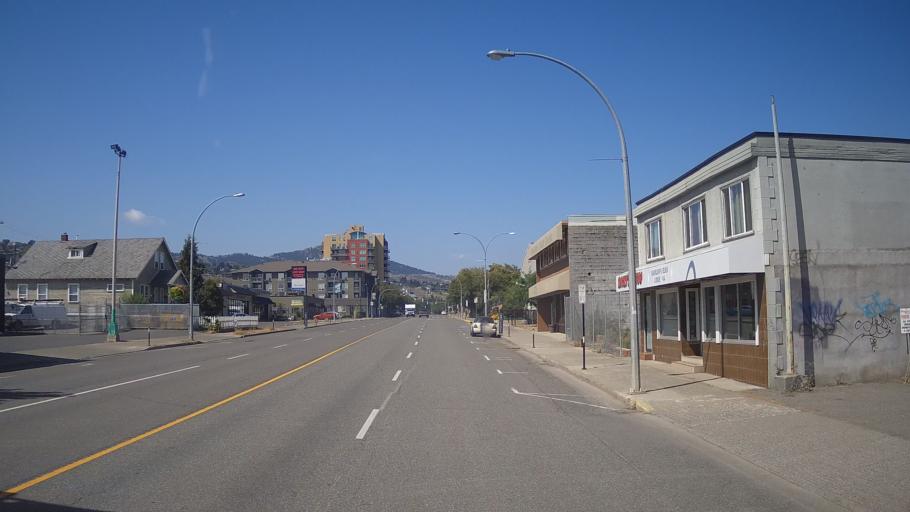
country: CA
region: British Columbia
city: Kamloops
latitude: 50.6758
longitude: -120.3216
